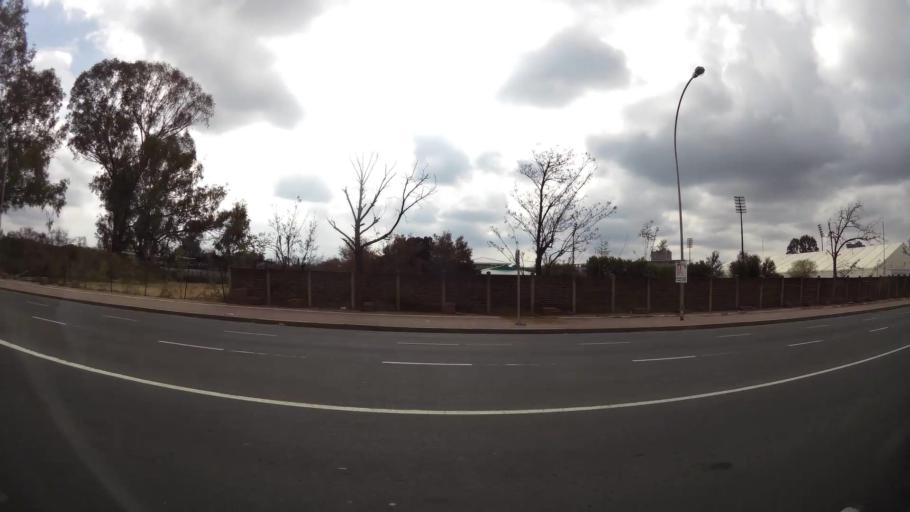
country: ZA
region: Orange Free State
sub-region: Mangaung Metropolitan Municipality
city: Bloemfontein
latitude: -29.1191
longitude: 26.2020
